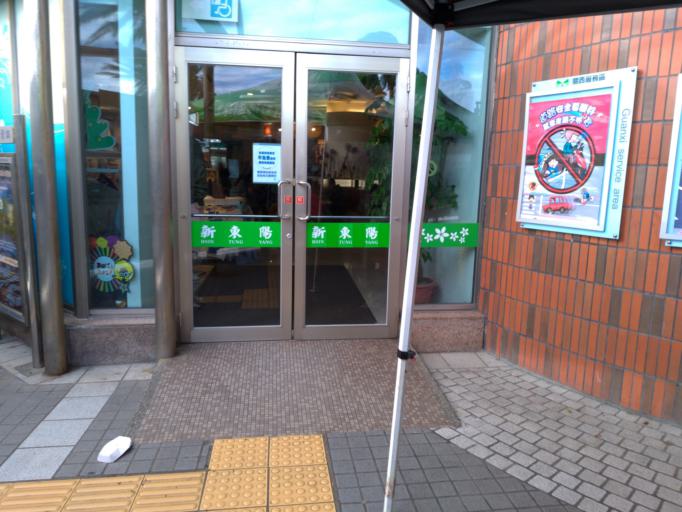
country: TW
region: Taiwan
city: Daxi
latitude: 24.8012
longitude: 121.1923
